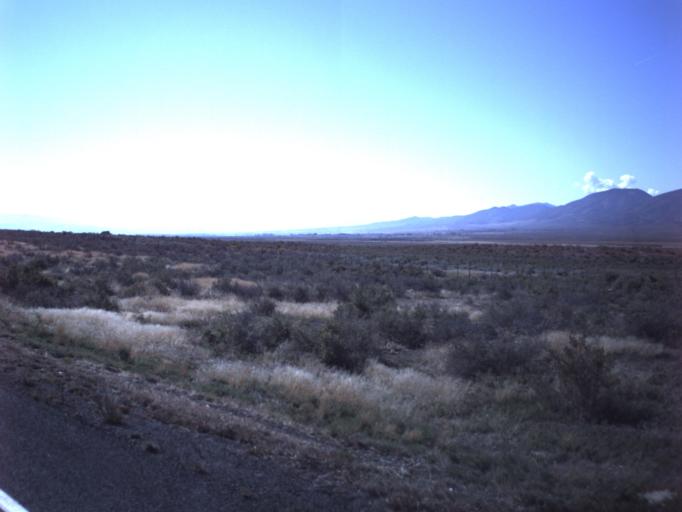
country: US
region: Utah
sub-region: Sanpete County
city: Gunnison
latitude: 39.2903
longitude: -111.8863
